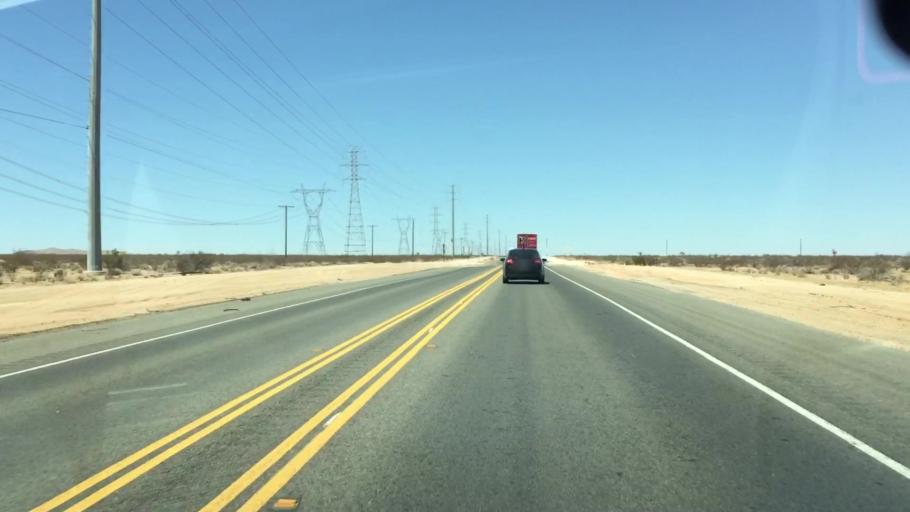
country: US
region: California
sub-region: San Bernardino County
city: Adelanto
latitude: 34.6990
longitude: -117.4530
